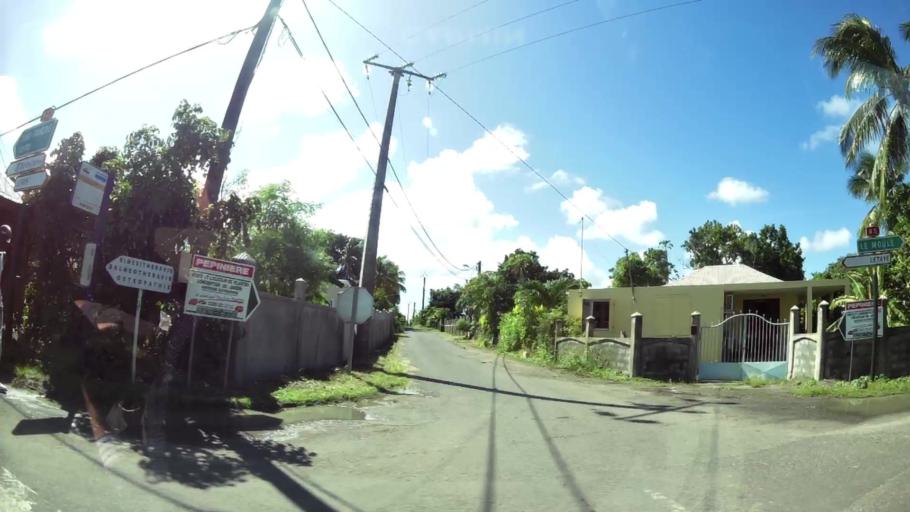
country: GP
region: Guadeloupe
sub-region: Guadeloupe
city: Saint-Francois
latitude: 16.2974
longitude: -61.2917
